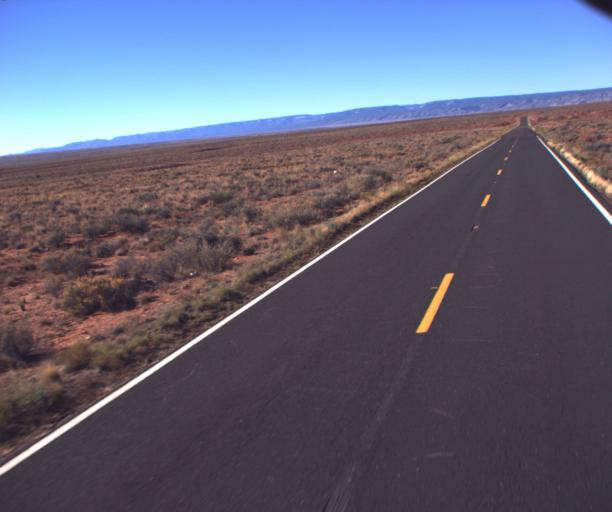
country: US
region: Arizona
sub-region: Coconino County
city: LeChee
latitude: 36.6940
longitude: -111.8128
